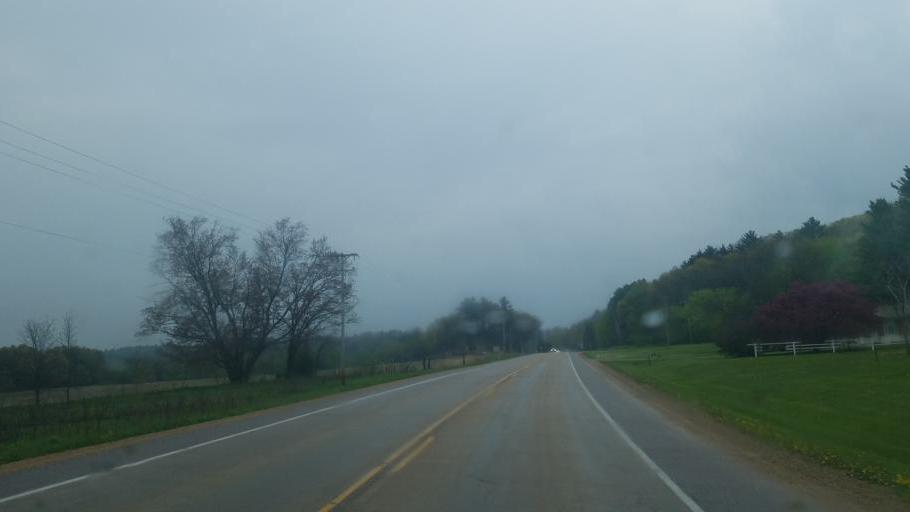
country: US
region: Wisconsin
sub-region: Juneau County
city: Elroy
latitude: 43.6370
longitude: -90.1809
